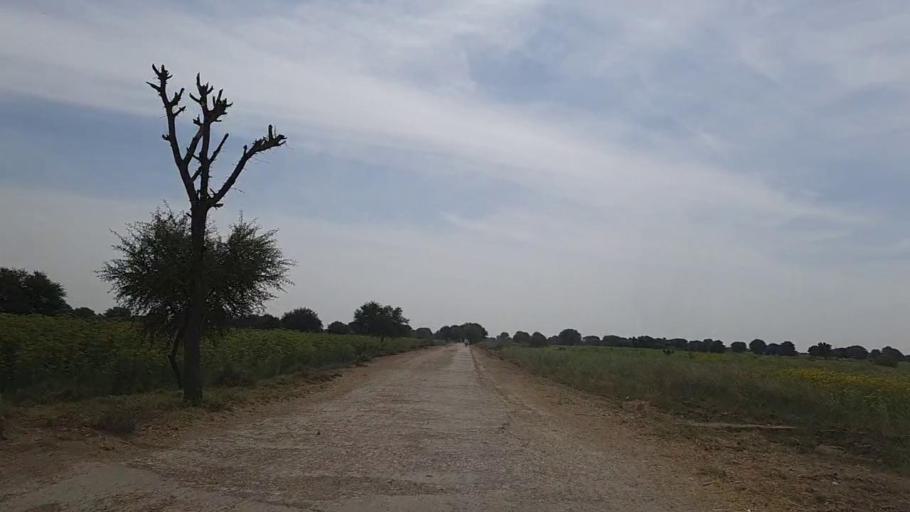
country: PK
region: Sindh
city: Samaro
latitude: 25.2845
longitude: 69.4537
